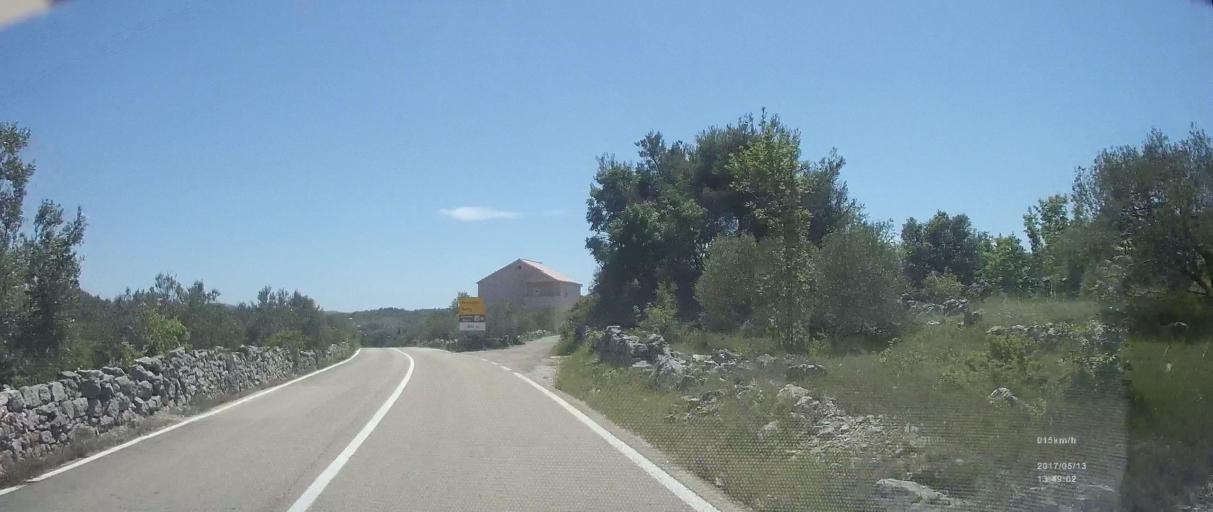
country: HR
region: Sibensko-Kniniska
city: Primosten
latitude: 43.6128
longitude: 15.9762
